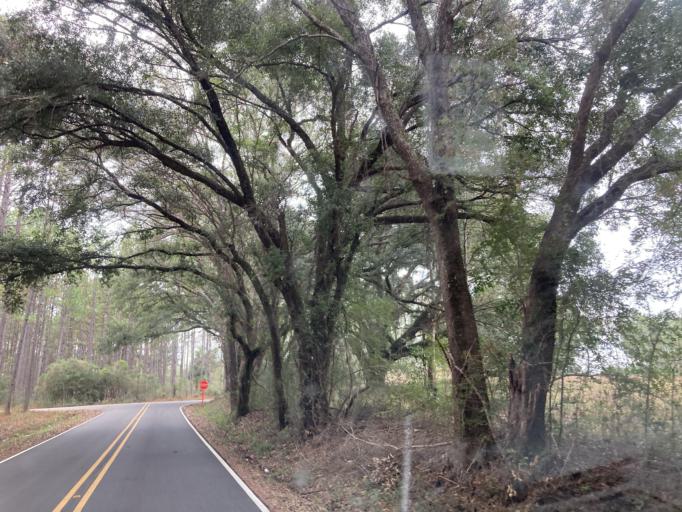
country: US
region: Mississippi
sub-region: Lamar County
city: Purvis
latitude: 31.1112
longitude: -89.4276
